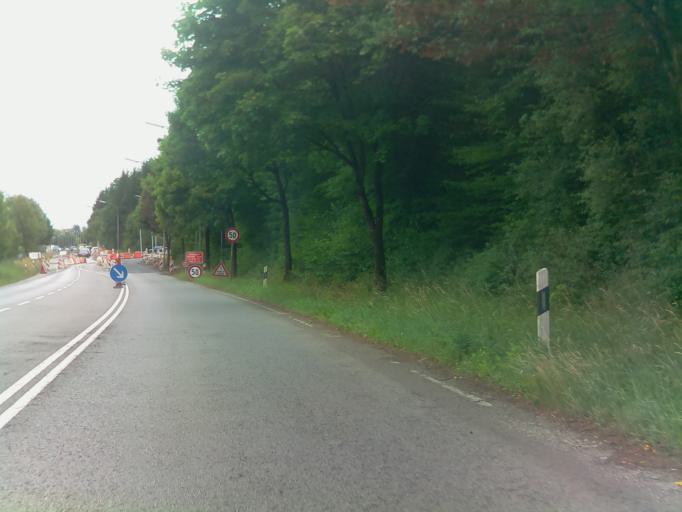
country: LU
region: Luxembourg
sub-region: Canton d'Esch-sur-Alzette
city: Bettembourg
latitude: 49.5052
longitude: 6.1310
